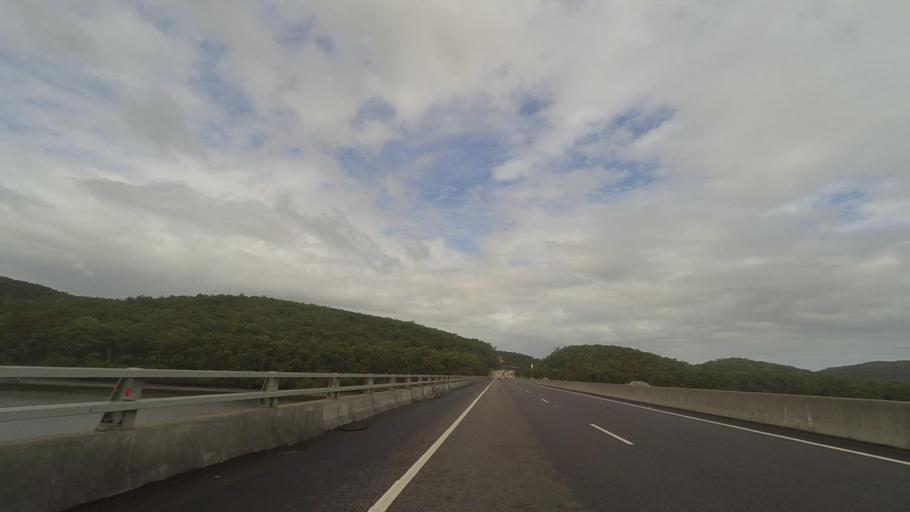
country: AU
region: New South Wales
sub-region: Port Stephens Shire
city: Port Stephens
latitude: -32.6216
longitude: 151.9595
